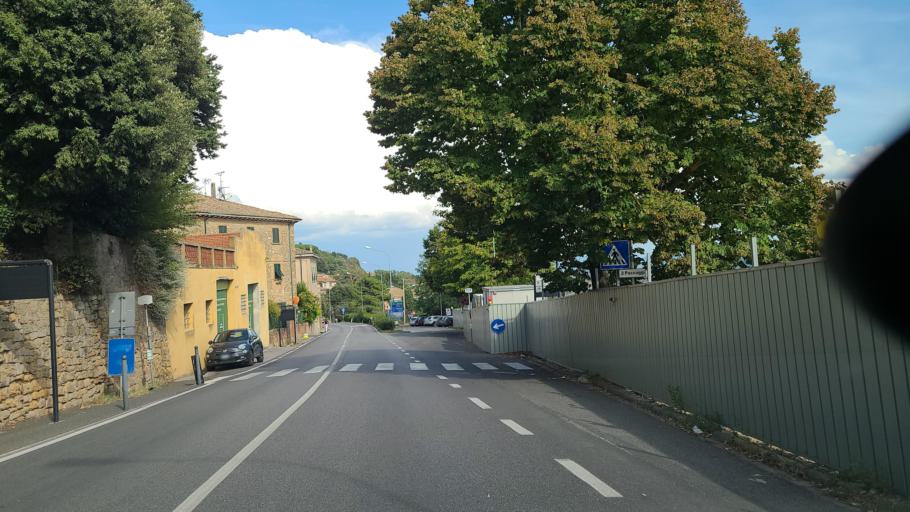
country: IT
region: Tuscany
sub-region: Province of Pisa
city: Volterra
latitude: 43.3993
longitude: 10.8661
